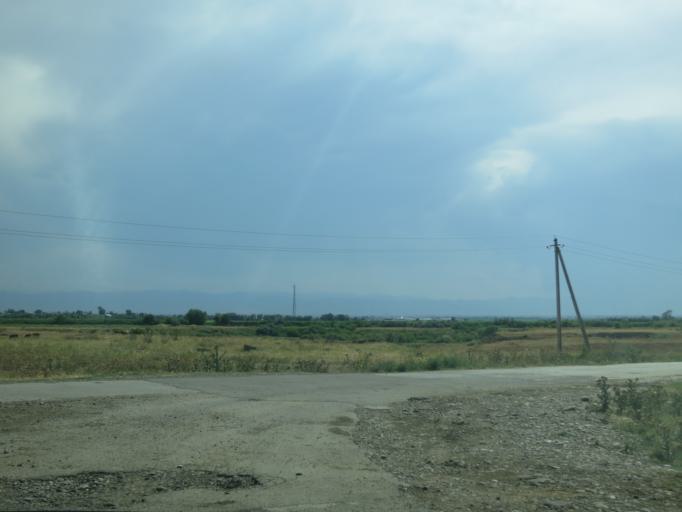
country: GE
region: Kvemo Kartli
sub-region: Gardabani
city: Gardabani
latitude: 41.4727
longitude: 45.1699
